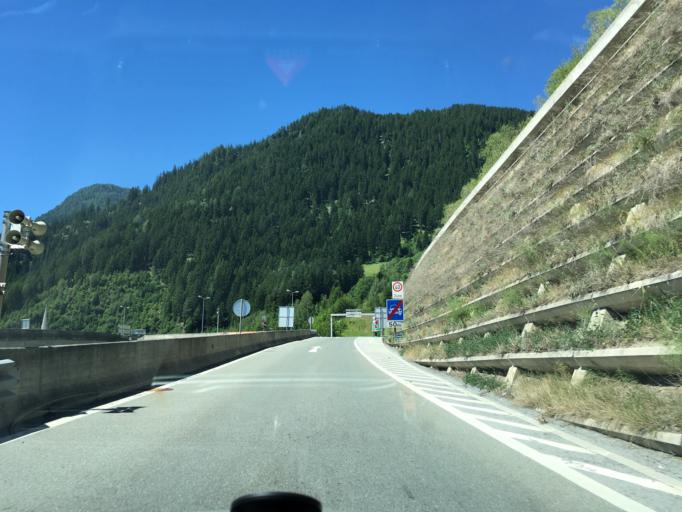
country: AT
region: Tyrol
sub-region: Politischer Bezirk Landeck
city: Pians
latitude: 47.1317
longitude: 10.5011
